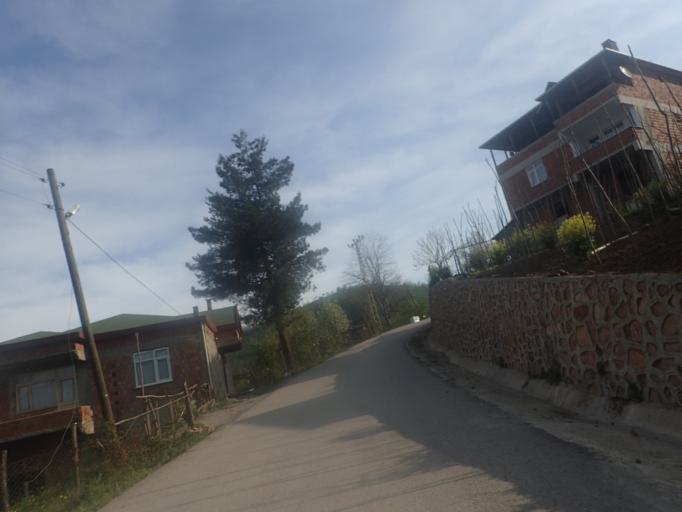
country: TR
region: Ordu
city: Catalpinar
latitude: 40.8785
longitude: 37.4759
